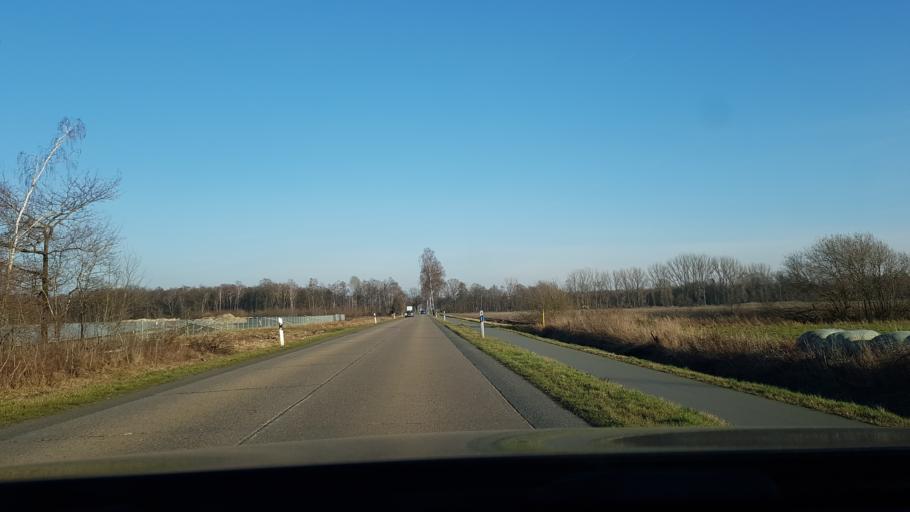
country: DE
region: Lower Saxony
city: Sassenburg
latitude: 52.5065
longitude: 10.5939
